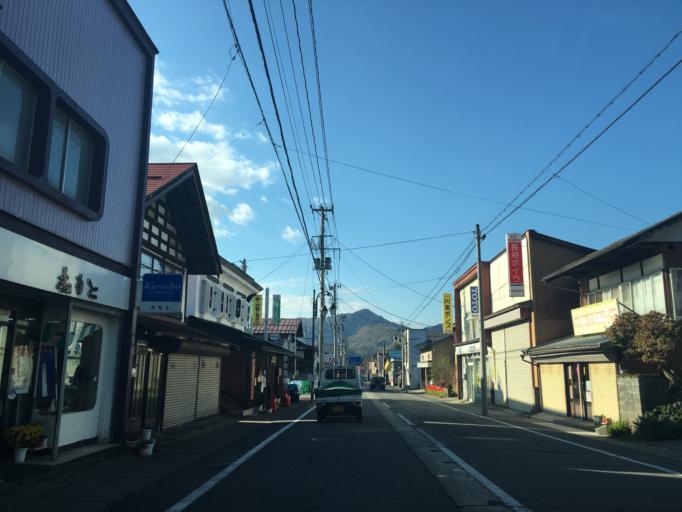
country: JP
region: Fukushima
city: Kitakata
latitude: 37.5857
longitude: 139.6469
